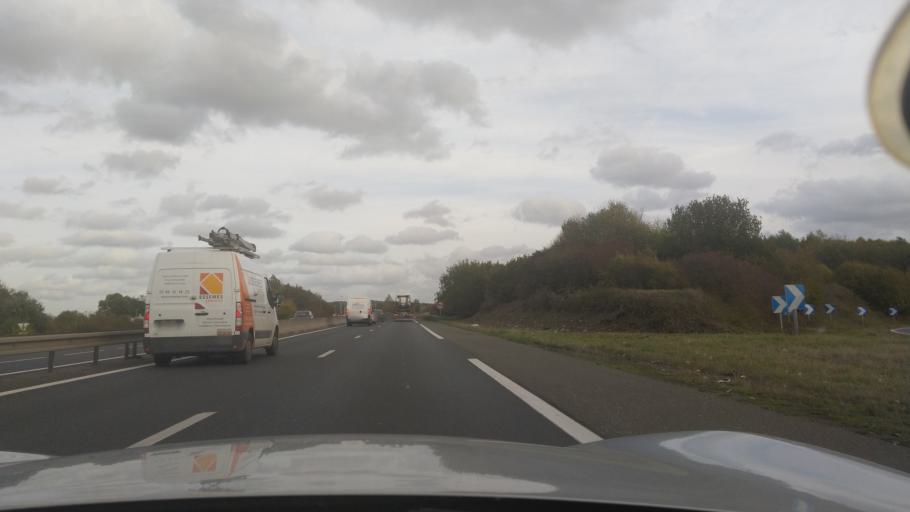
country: FR
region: Ile-de-France
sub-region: Departement du Val-d'Oise
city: Mery-sur-Oise
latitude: 49.0522
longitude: 2.1804
